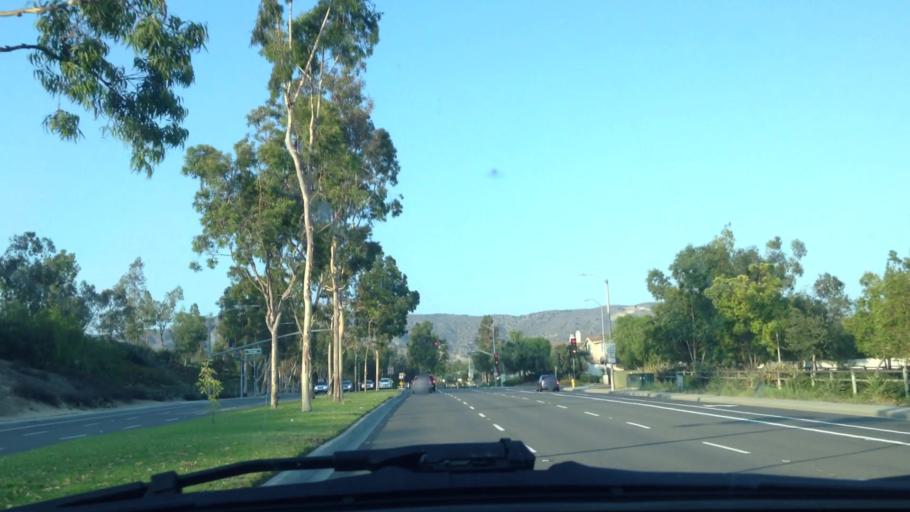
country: US
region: California
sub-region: Orange County
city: North Tustin
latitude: 33.7467
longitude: -117.7753
